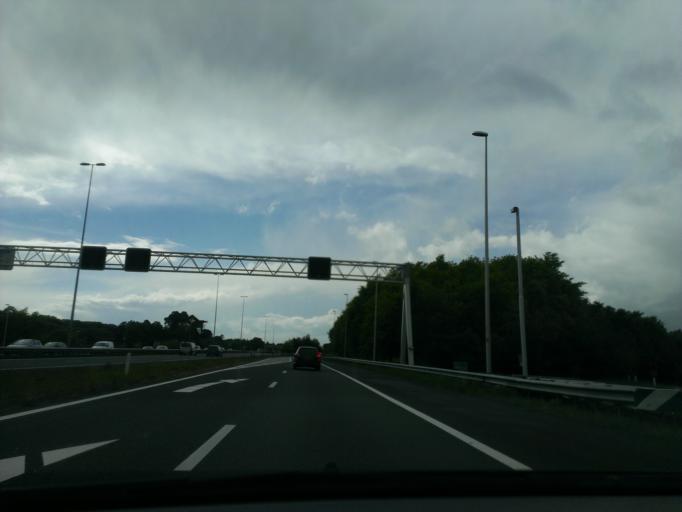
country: NL
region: Gelderland
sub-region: Gemeente Rozendaal
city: Rozendaal
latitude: 52.0152
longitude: 5.9291
